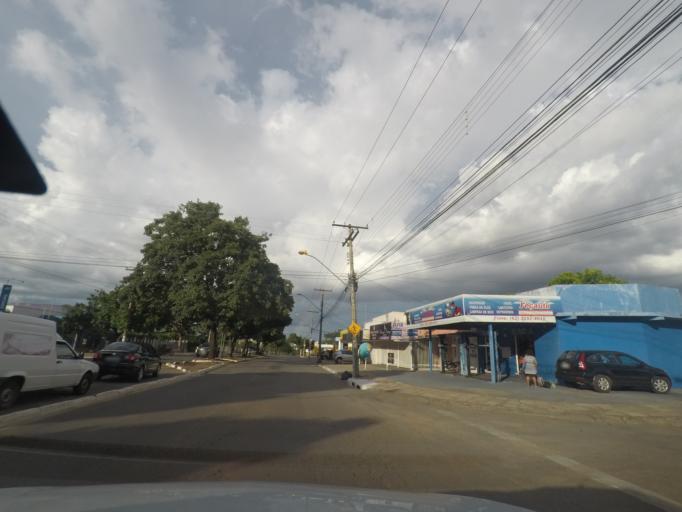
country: BR
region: Goias
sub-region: Goiania
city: Goiania
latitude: -16.6800
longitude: -49.2988
